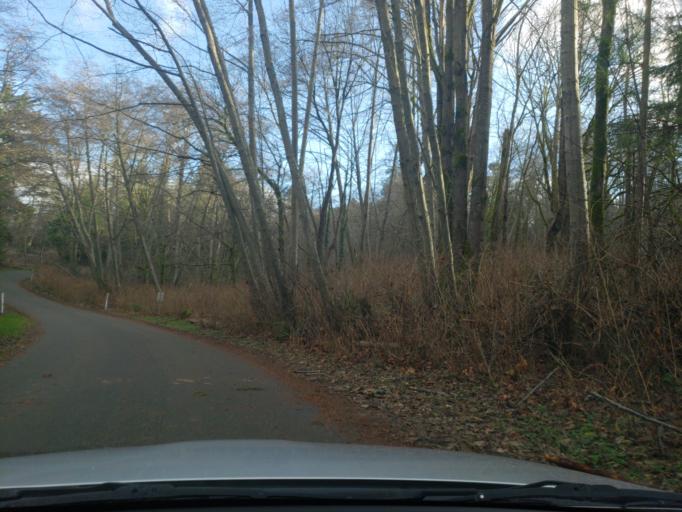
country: US
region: Washington
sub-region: King County
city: Seattle
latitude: 47.6676
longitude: -122.4130
